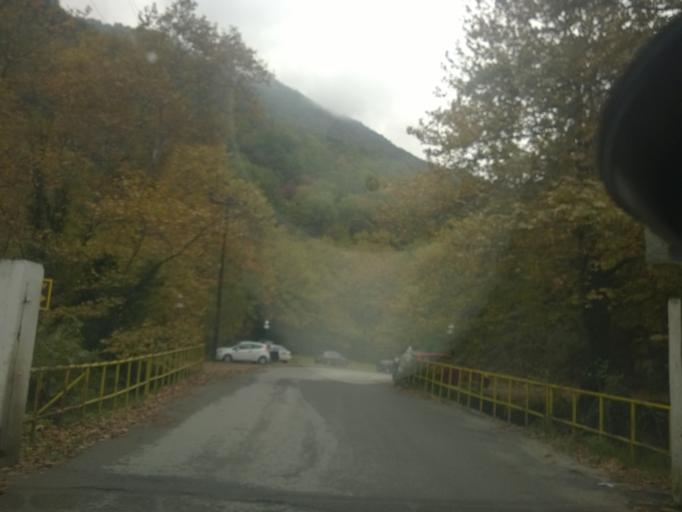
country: GR
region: Central Macedonia
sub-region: Nomos Pellis
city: Loutraki
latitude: 40.9708
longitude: 21.9172
